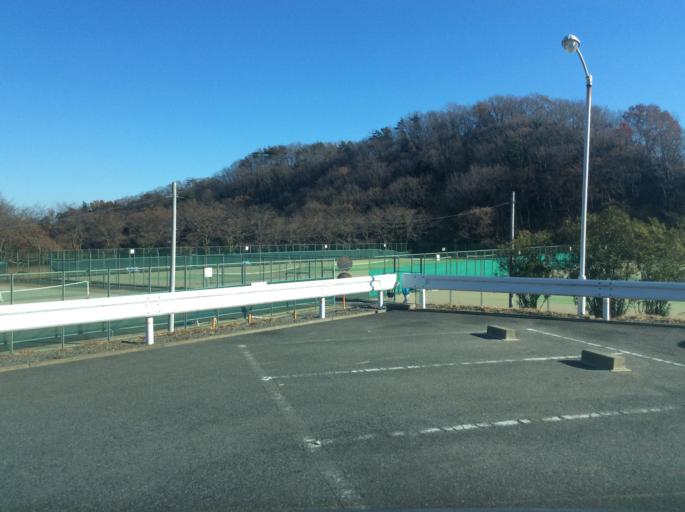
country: JP
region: Fukushima
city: Iwaki
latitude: 37.0201
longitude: 140.9186
